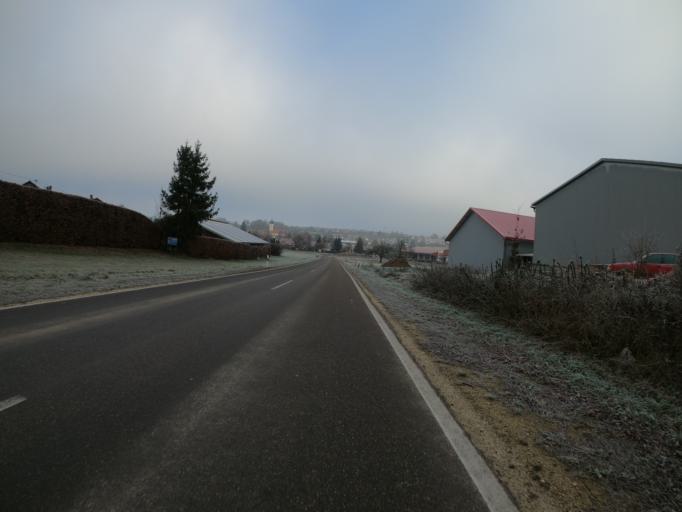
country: DE
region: Baden-Wuerttemberg
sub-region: Tuebingen Region
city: Westerstetten
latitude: 48.5154
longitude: 9.9553
